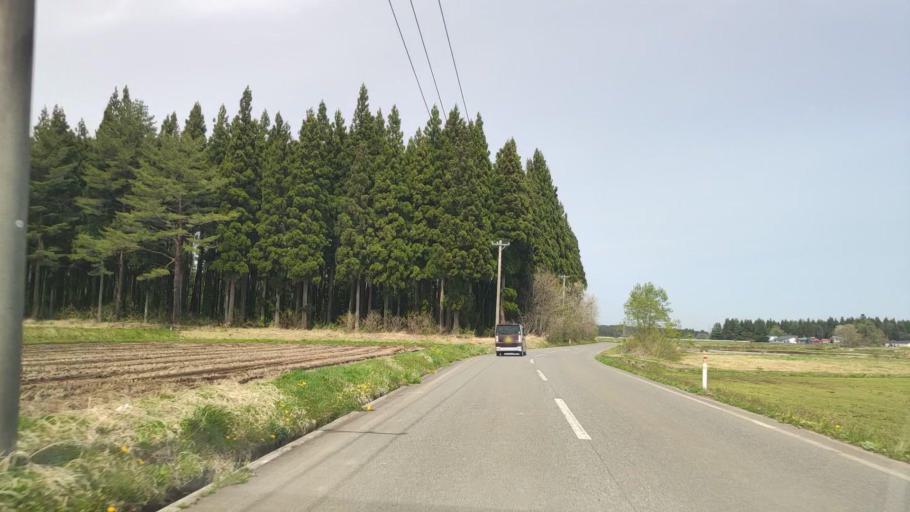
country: JP
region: Aomori
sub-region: Misawa Shi
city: Inuotose
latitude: 40.7682
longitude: 141.1215
